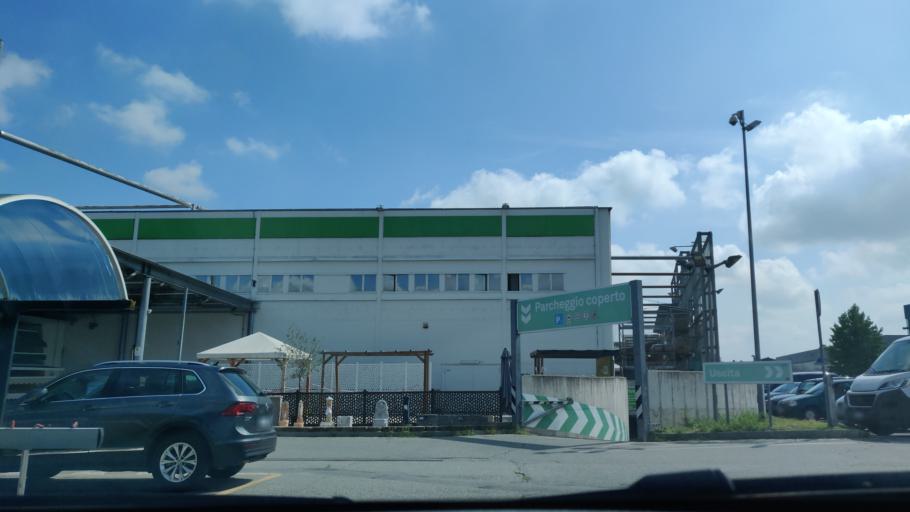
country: IT
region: Piedmont
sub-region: Provincia di Torino
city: Savonera
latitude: 45.1016
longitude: 7.5950
